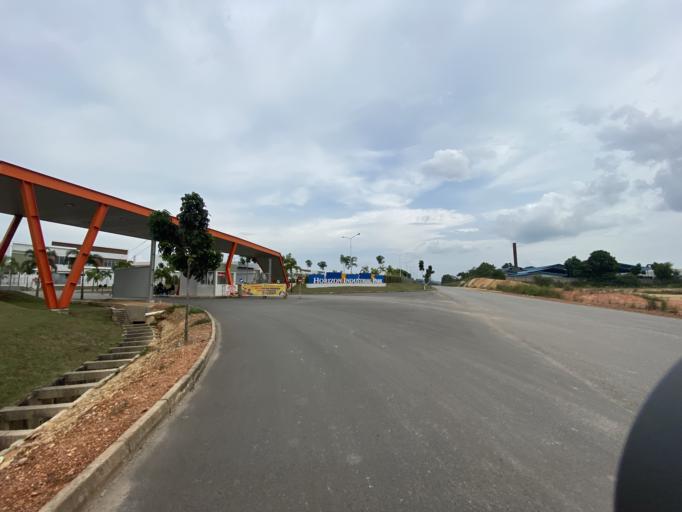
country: SG
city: Singapore
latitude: 1.0216
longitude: 103.9465
